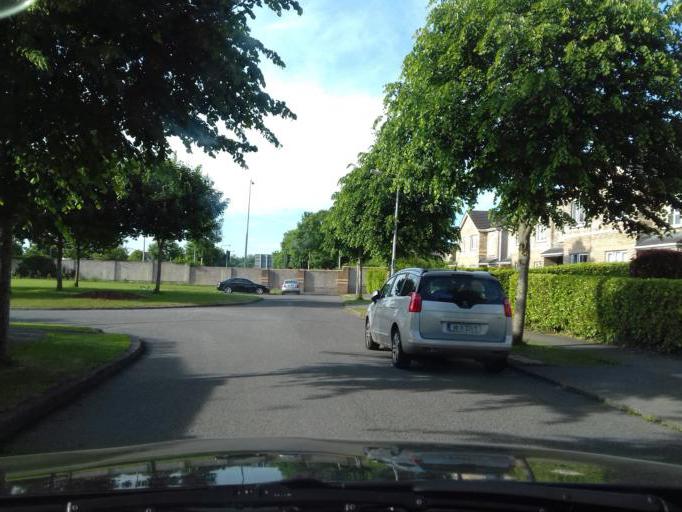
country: IE
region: Leinster
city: Hartstown
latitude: 53.3868
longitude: -6.4143
